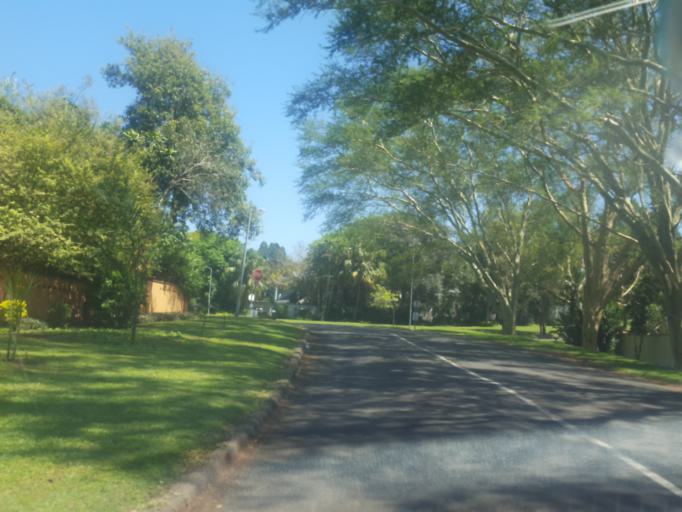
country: ZA
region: KwaZulu-Natal
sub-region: uThungulu District Municipality
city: Empangeni
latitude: -28.7439
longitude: 31.9026
